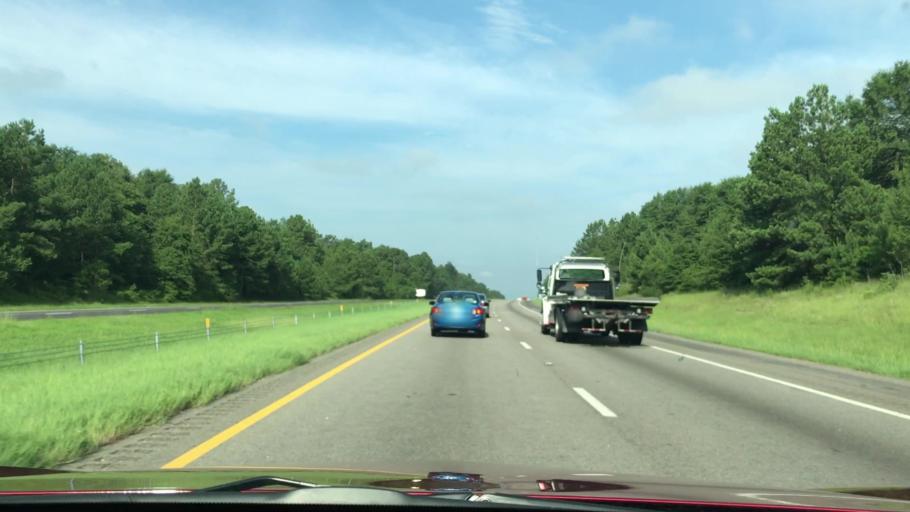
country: US
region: South Carolina
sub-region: Aiken County
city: Aiken
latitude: 33.6369
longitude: -81.7495
